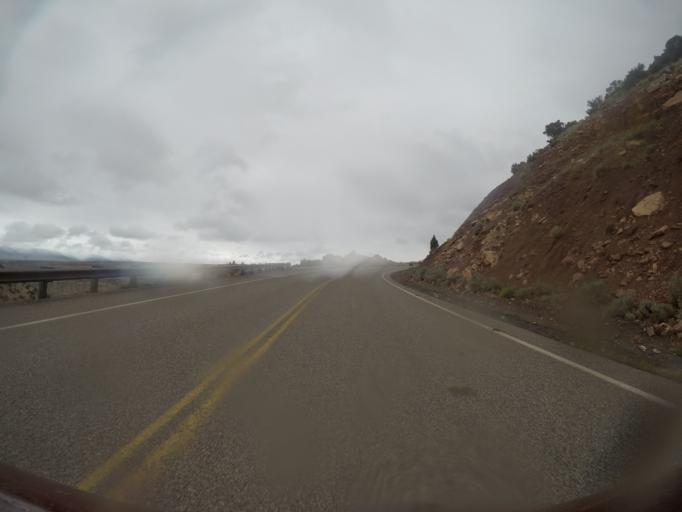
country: US
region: Wyoming
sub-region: Big Horn County
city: Lovell
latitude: 45.0452
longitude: -108.2530
